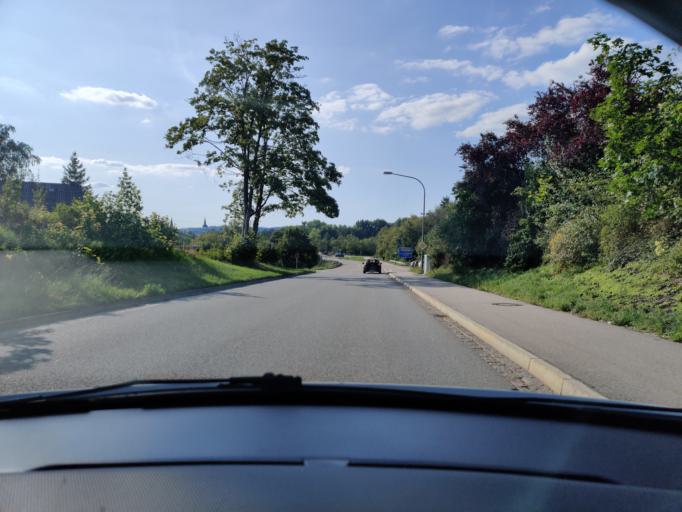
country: DE
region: Bavaria
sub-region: Upper Palatinate
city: Schwarzenfeld
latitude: 49.3870
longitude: 12.1518
